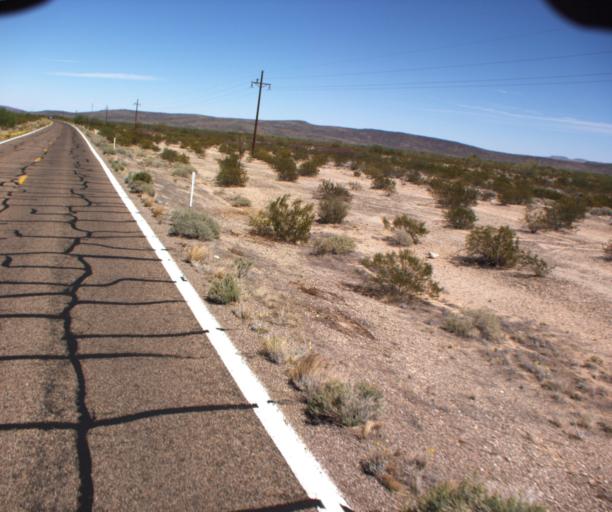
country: US
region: Arizona
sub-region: Pima County
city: Ajo
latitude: 32.4438
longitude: -112.8710
